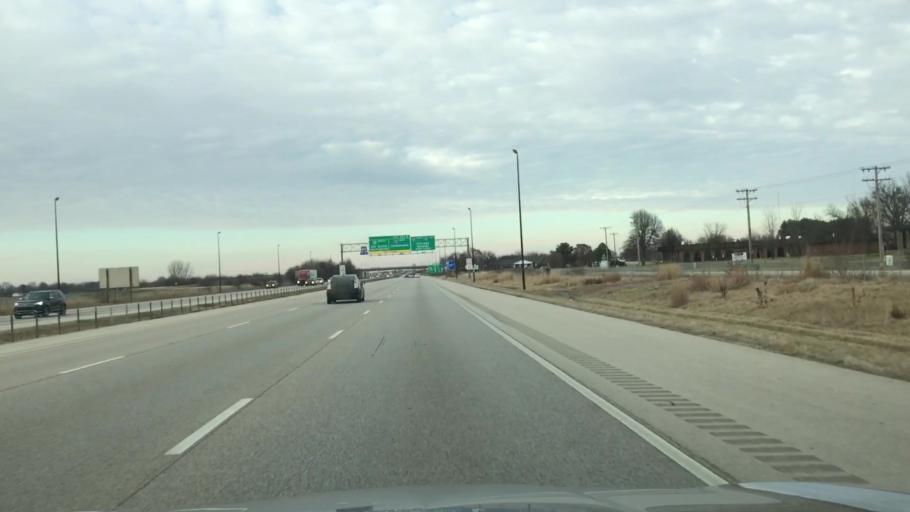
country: US
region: Illinois
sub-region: Sangamon County
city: Southern View
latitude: 39.7228
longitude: -89.6438
